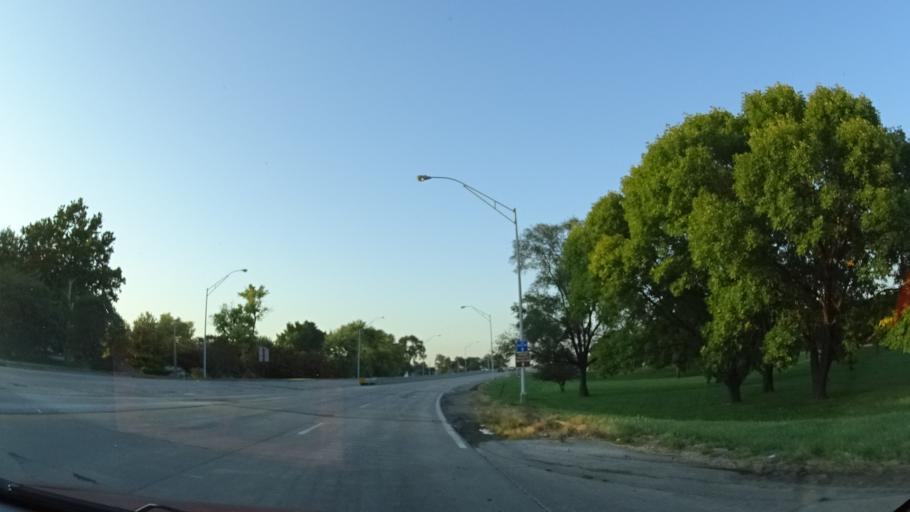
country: US
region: Iowa
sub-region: Pottawattamie County
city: Council Bluffs
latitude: 41.2440
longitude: -95.8536
